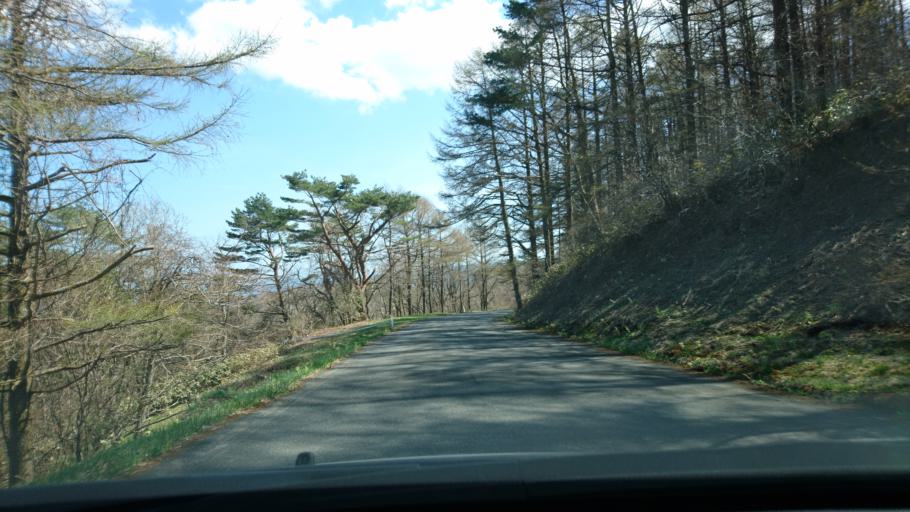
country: JP
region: Iwate
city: Ofunato
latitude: 38.9753
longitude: 141.4571
